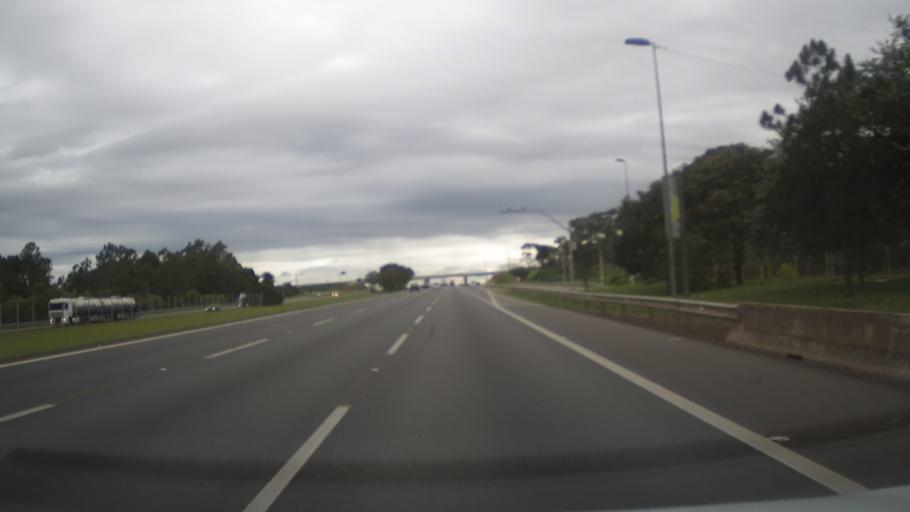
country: BR
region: Sao Paulo
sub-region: Valinhos
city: Valinhos
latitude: -23.0112
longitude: -47.0898
